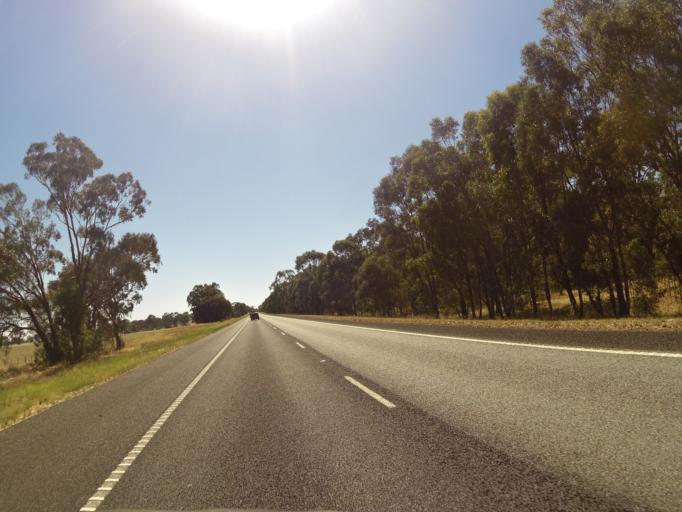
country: AU
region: Victoria
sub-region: Greater Shepparton
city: Shepparton
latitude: -36.8398
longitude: 145.3649
